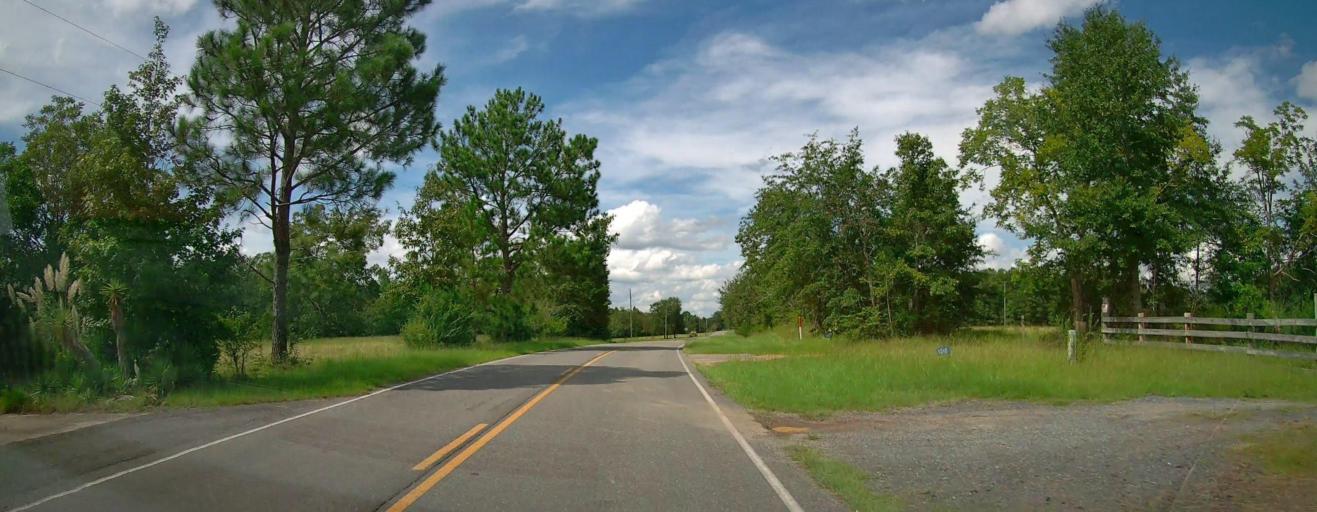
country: US
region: Georgia
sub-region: Taylor County
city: Butler
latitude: 32.4732
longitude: -84.2029
